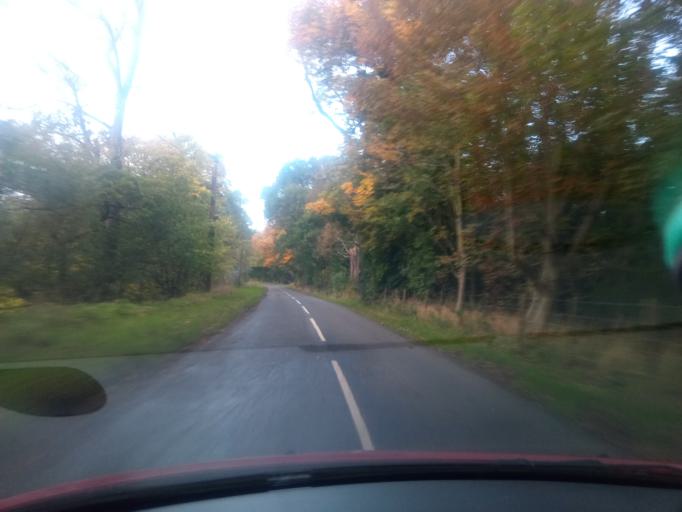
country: GB
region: Scotland
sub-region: The Scottish Borders
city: Jedburgh
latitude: 55.4134
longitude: -2.6432
